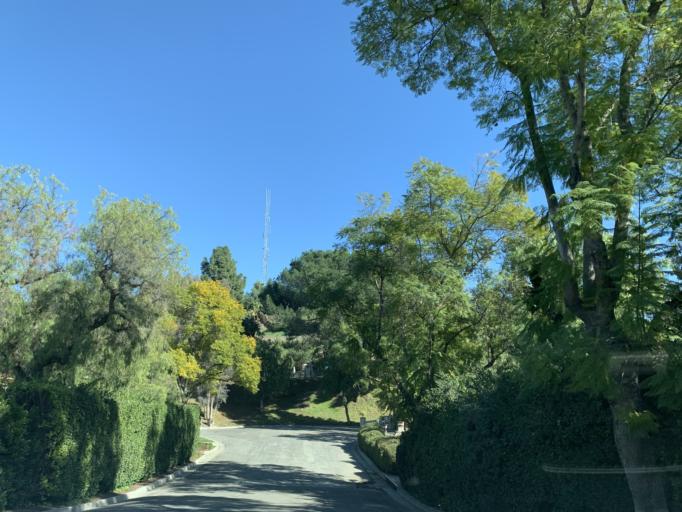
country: US
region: California
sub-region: Orange County
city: Brea
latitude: 33.8918
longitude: -117.9043
